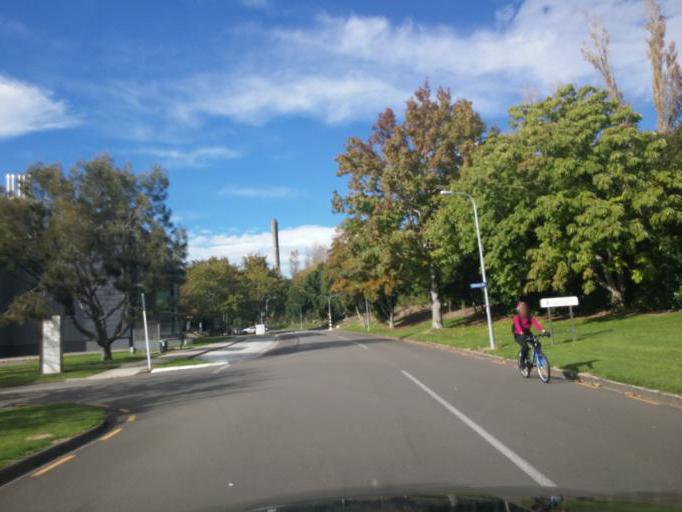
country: NZ
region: Manawatu-Wanganui
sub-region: Palmerston North City
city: Palmerston North
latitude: -40.3865
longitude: 175.6150
